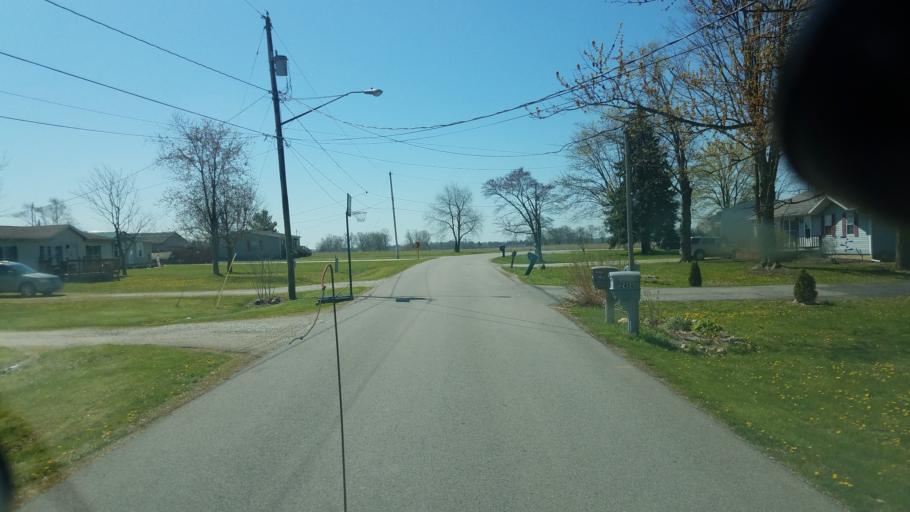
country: US
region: Ohio
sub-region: Marion County
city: Marion
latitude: 40.6368
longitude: -83.0753
